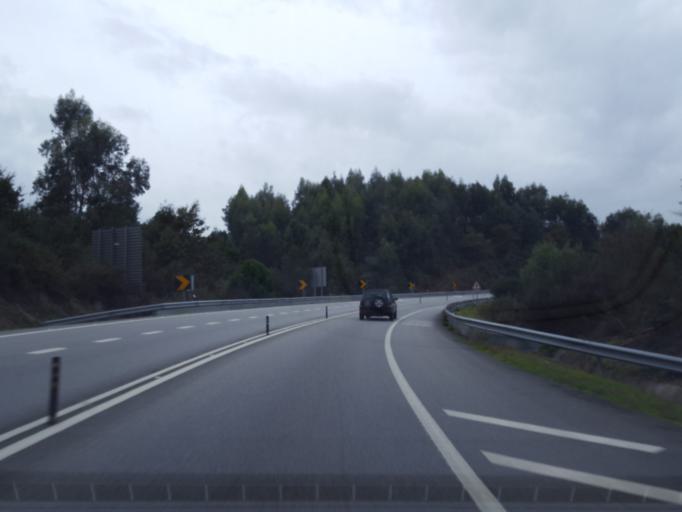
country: PT
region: Porto
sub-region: Marco de Canaveses
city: Marco de Canavezes
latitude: 41.2220
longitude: -8.1892
